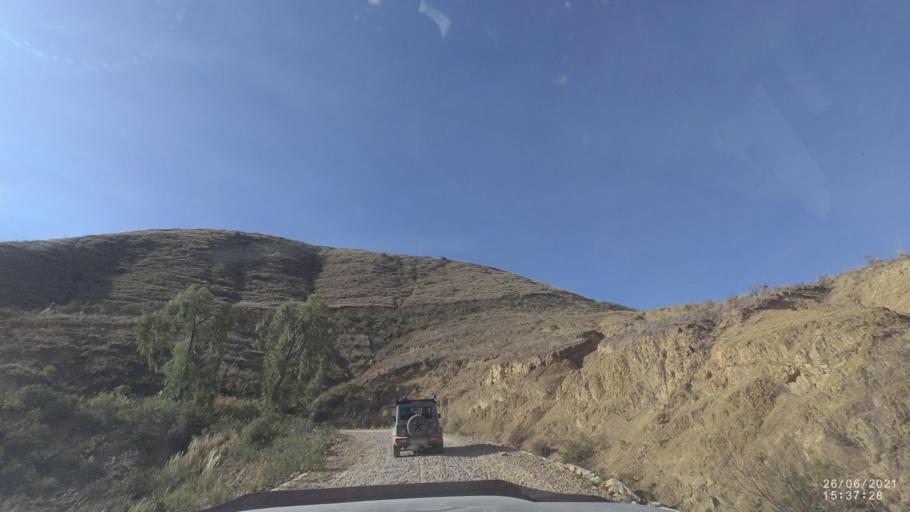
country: BO
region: Cochabamba
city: Mizque
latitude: -17.9125
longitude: -65.6878
